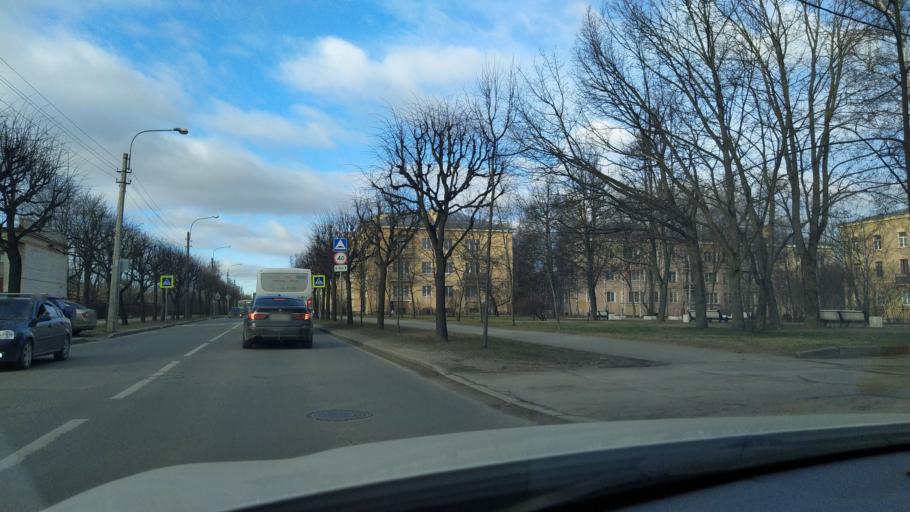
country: RU
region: St.-Petersburg
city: Pushkin
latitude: 59.7243
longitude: 30.4247
